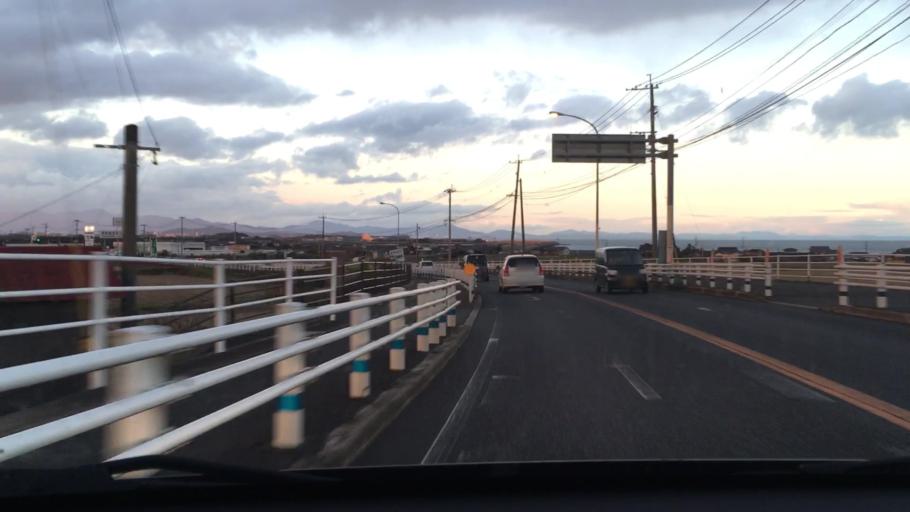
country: JP
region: Fukuoka
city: Shiida
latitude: 33.6275
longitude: 131.0877
